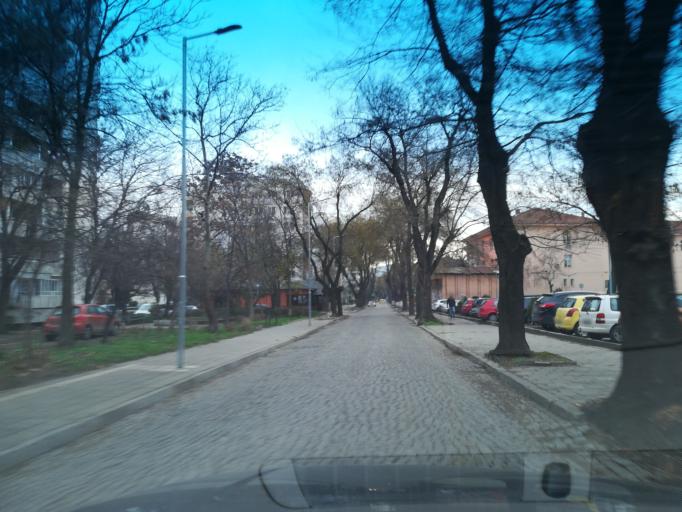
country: BG
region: Plovdiv
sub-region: Obshtina Plovdiv
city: Plovdiv
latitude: 42.1424
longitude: 24.7592
